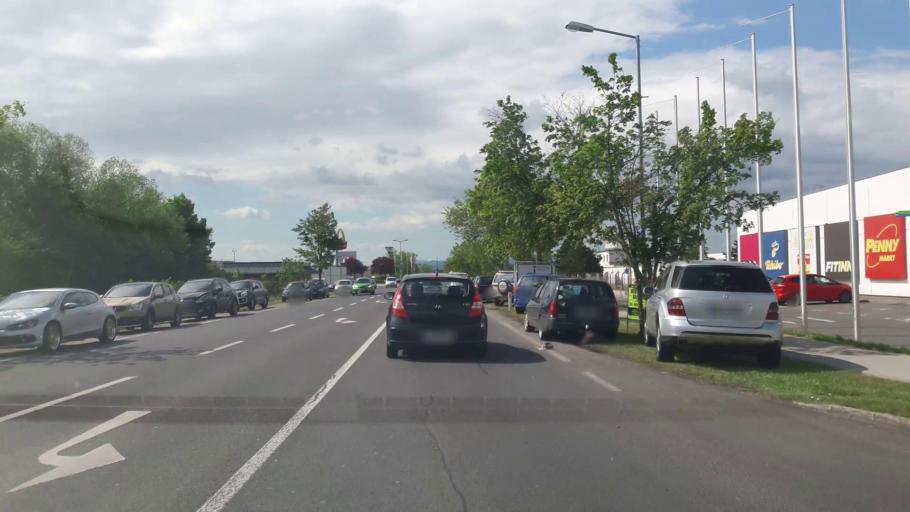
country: AT
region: Lower Austria
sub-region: Politischer Bezirk Wiener Neustadt
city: Theresienfeld
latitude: 47.8451
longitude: 16.2459
